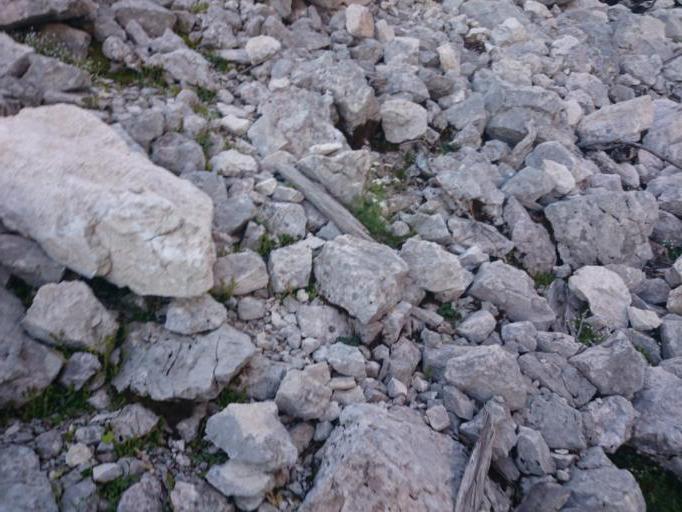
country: AL
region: Elbasan
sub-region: Rrethi i Gramshit
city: Kushove
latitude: 40.7199
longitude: 20.1447
